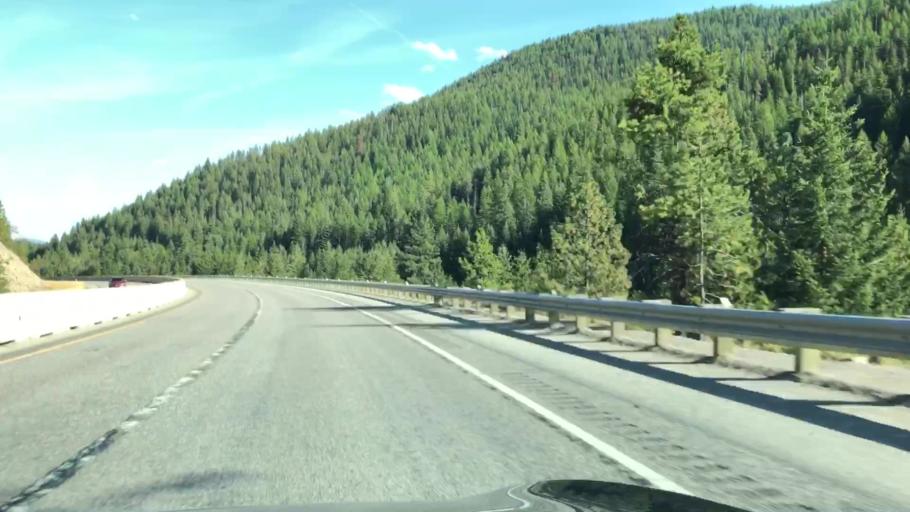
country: US
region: Montana
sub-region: Sanders County
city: Thompson Falls
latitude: 47.3947
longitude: -115.4527
